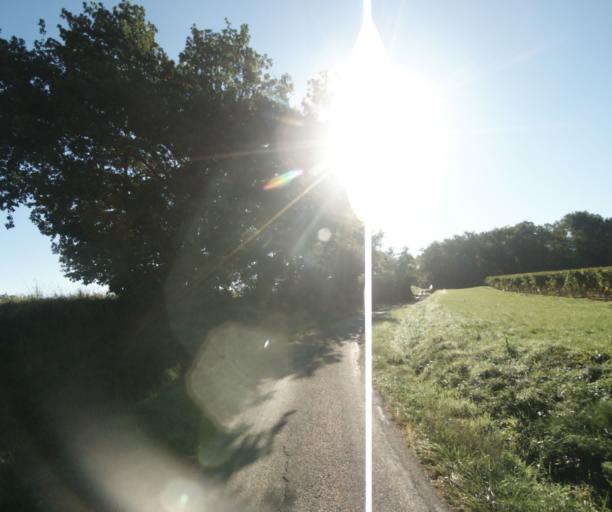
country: FR
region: Midi-Pyrenees
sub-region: Departement du Gers
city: Gondrin
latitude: 43.8412
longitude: 0.2660
